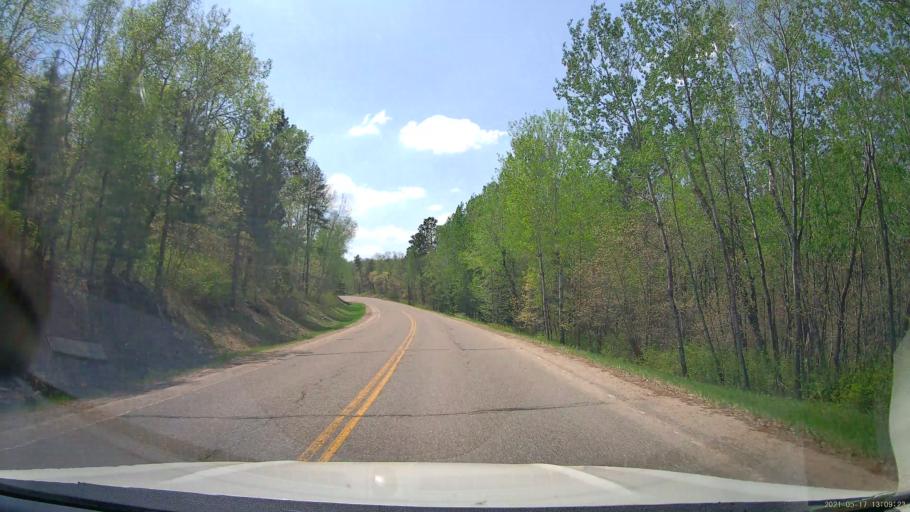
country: US
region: Minnesota
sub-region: Hubbard County
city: Park Rapids
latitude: 47.0276
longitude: -94.9283
